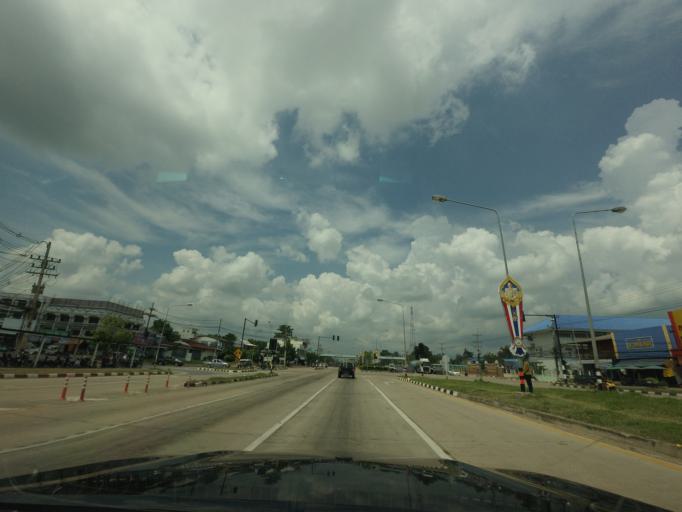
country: TH
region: Khon Kaen
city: Nong Ruea
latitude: 16.4914
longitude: 102.4355
